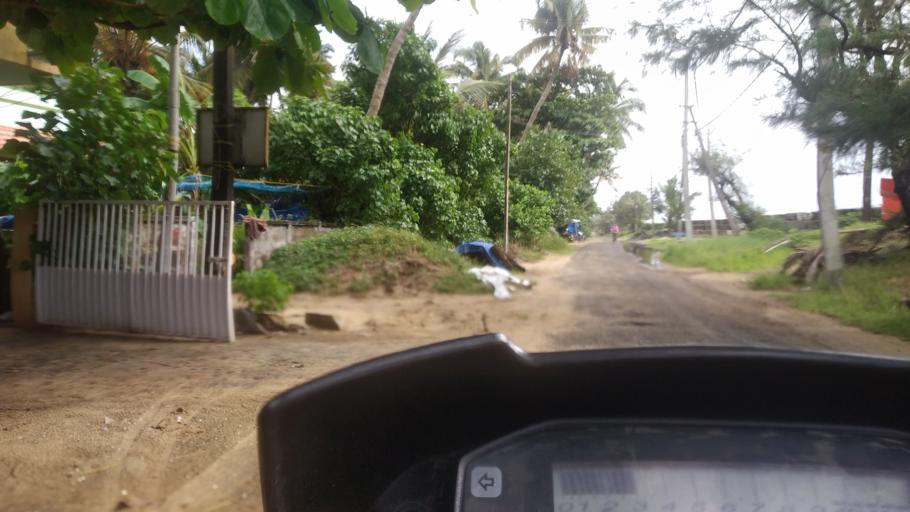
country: IN
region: Kerala
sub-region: Thrissur District
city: Kodungallur
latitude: 10.1347
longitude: 76.1808
